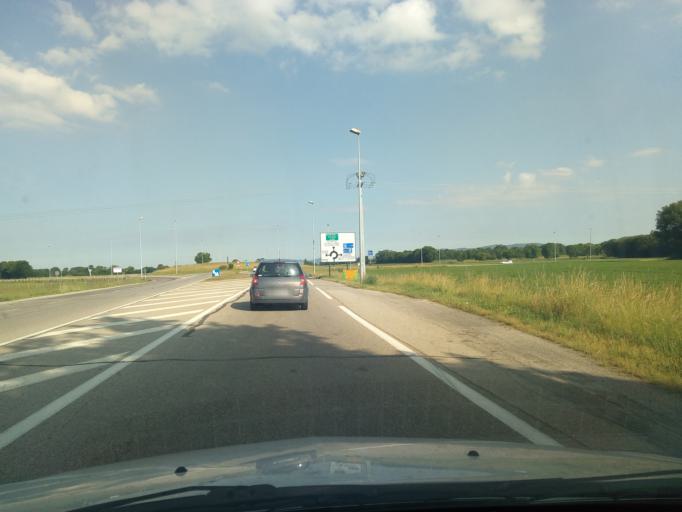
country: FR
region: Rhone-Alpes
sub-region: Departement de l'Isere
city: Beaucroissant
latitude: 45.3476
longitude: 5.4703
